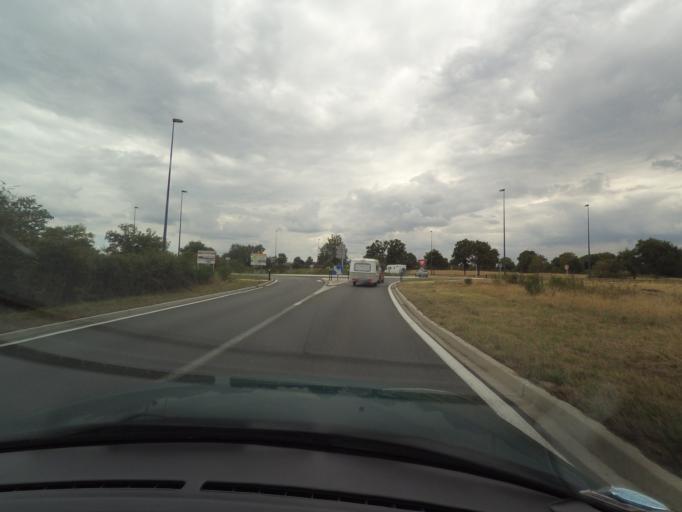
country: FR
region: Poitou-Charentes
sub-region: Departement des Deux-Sevres
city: Viennay
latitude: 46.6711
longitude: -0.2567
